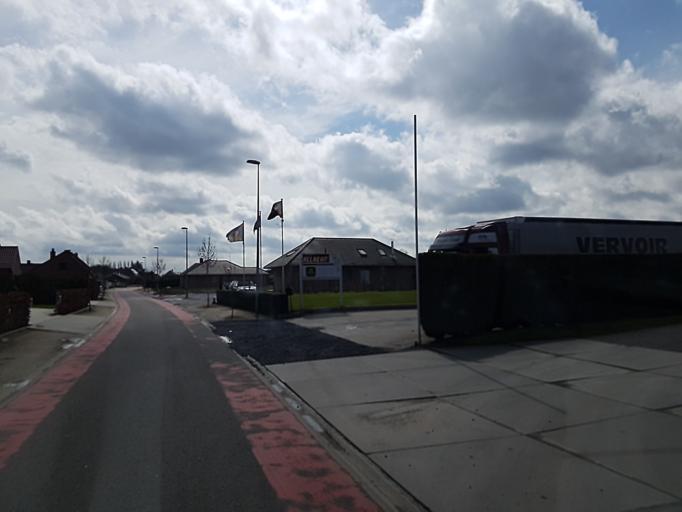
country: BE
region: Flanders
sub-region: Provincie Oost-Vlaanderen
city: Deinze
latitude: 50.9520
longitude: 3.4917
